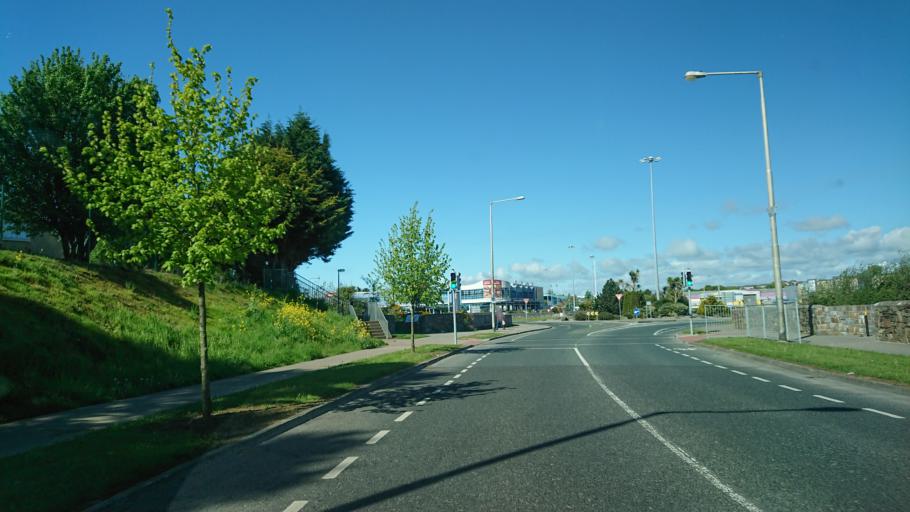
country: IE
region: Munster
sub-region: Waterford
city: Waterford
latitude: 52.2471
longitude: -7.1181
